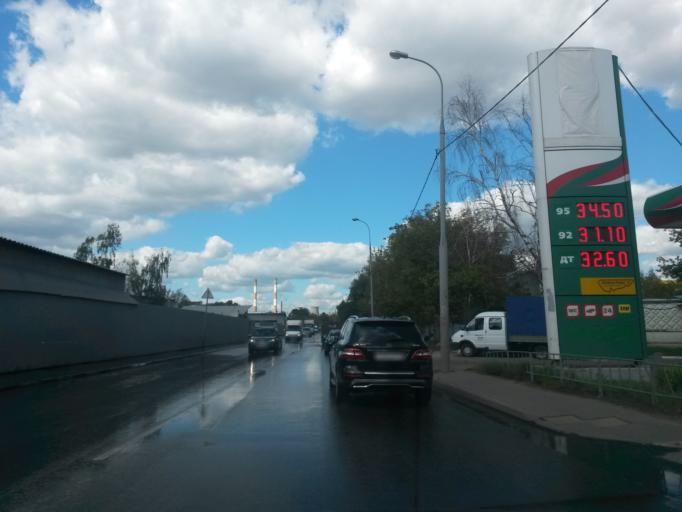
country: RU
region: Moskovskaya
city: Kozhukhovo
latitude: 55.7042
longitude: 37.7027
